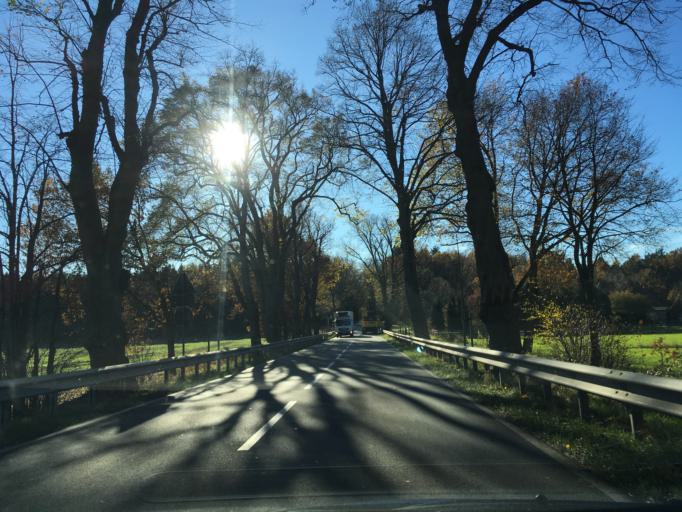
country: DE
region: Lower Saxony
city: Amelinghausen
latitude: 53.1127
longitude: 10.1773
